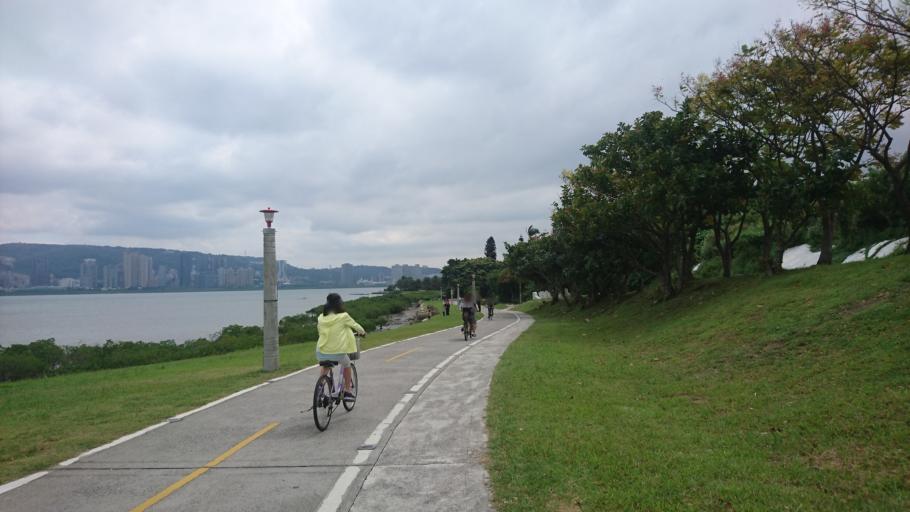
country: TW
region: Taipei
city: Taipei
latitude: 25.1571
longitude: 121.4370
